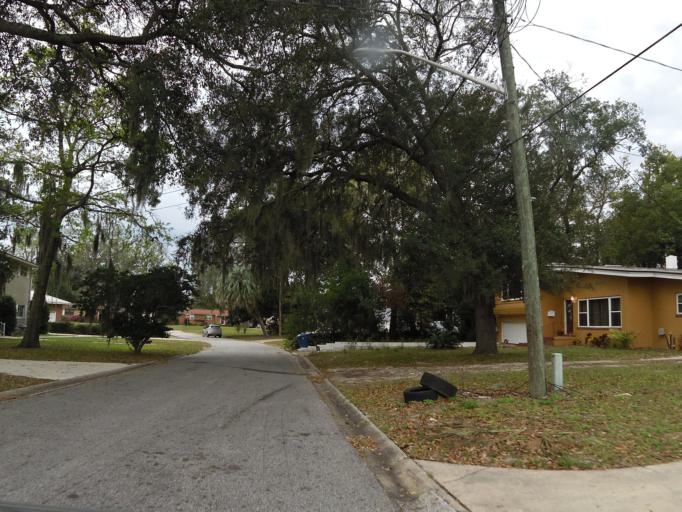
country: US
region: Florida
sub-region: Duval County
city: Jacksonville
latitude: 30.3316
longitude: -81.6084
